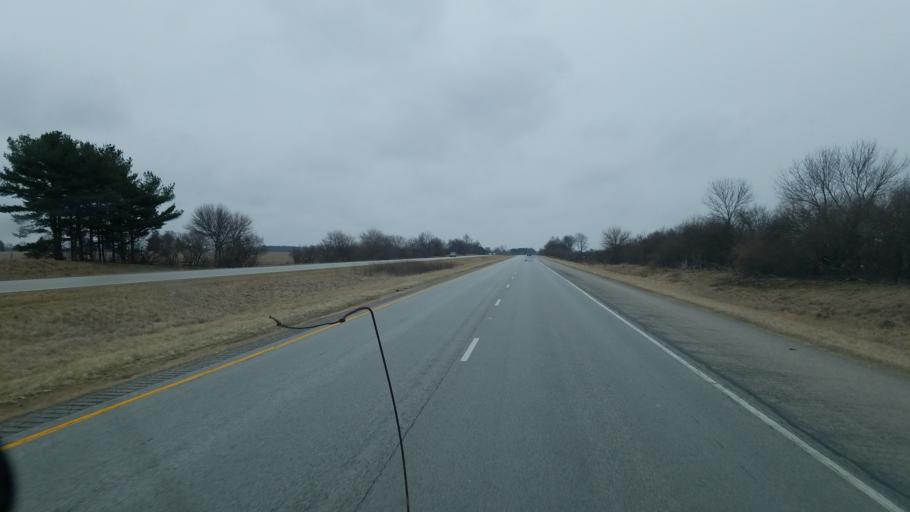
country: US
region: Indiana
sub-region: Fulton County
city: Rochester
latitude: 40.9281
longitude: -86.1659
